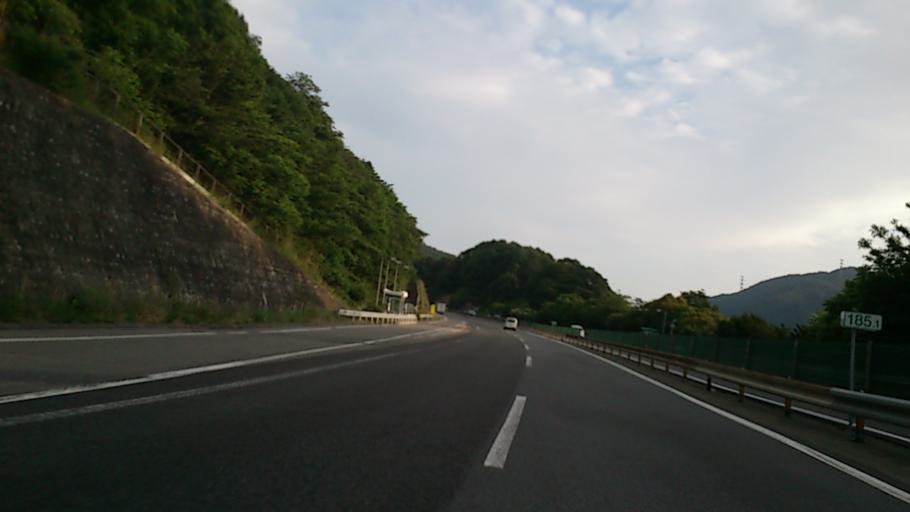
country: JP
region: Nagano
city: Okaya
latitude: 36.0326
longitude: 138.0232
